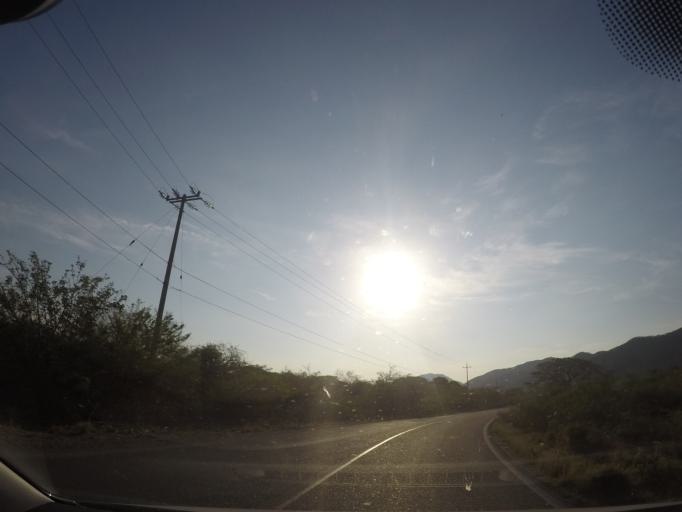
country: MX
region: Oaxaca
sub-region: Santo Domingo Tehuantepec
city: La Noria
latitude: 16.2309
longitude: -95.1831
